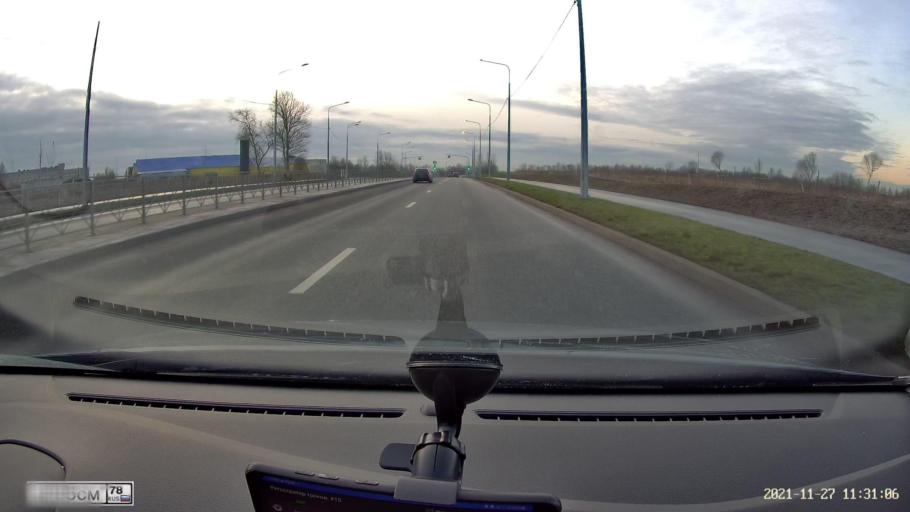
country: RU
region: St.-Petersburg
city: Krasnoye Selo
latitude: 59.7233
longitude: 30.0523
